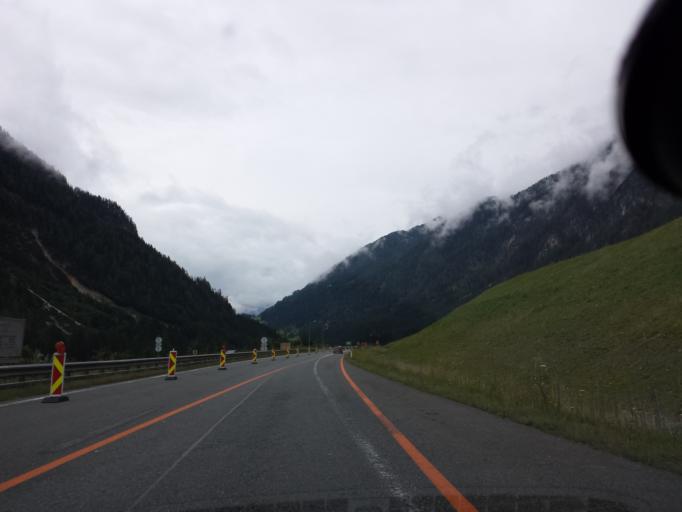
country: AT
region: Salzburg
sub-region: Politischer Bezirk Sankt Johann im Pongau
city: Flachau
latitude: 47.2630
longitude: 13.4155
